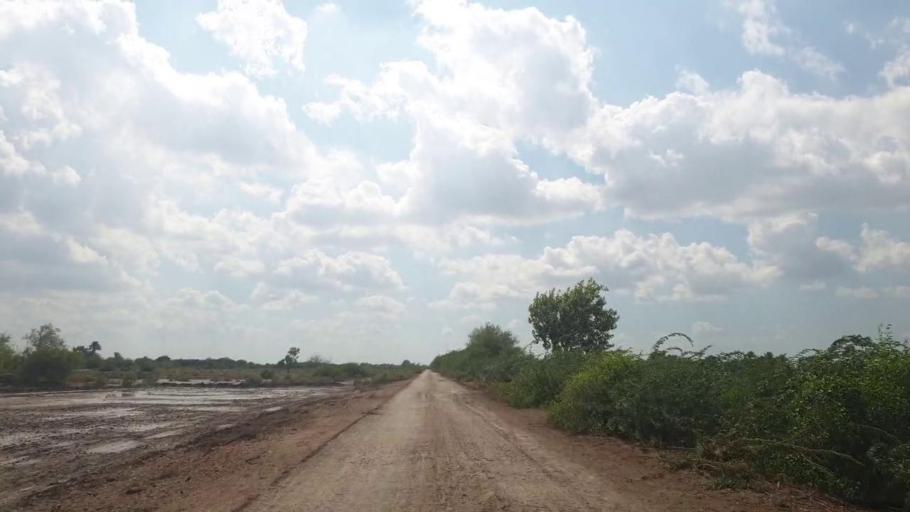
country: PK
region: Sindh
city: Pithoro
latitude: 25.5773
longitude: 69.3798
